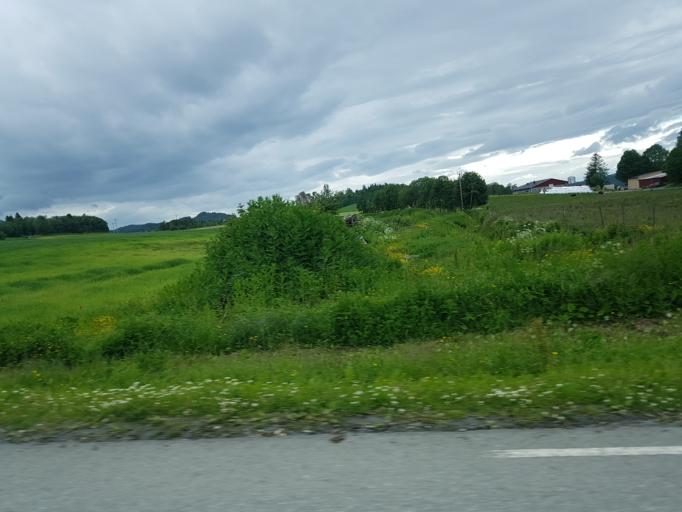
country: NO
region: Nord-Trondelag
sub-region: Levanger
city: Skogn
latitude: 63.6100
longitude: 11.0773
